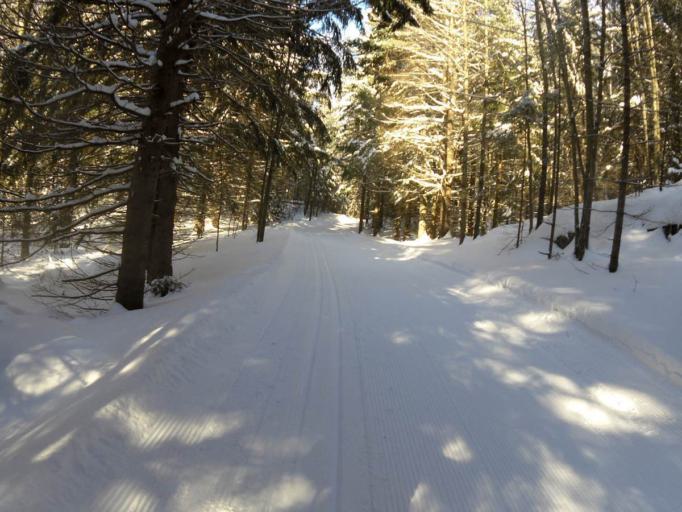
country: CA
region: Quebec
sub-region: Outaouais
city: Wakefield
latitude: 45.6215
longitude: -75.9461
